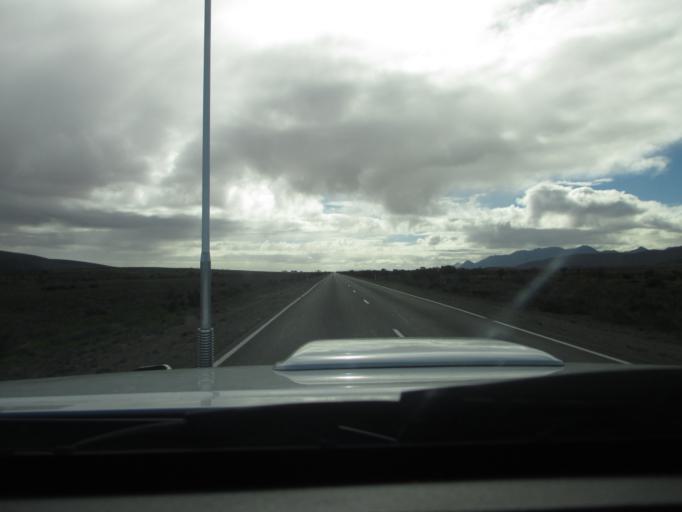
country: AU
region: South Australia
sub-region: Flinders Ranges
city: Quorn
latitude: -31.6448
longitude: 138.3824
